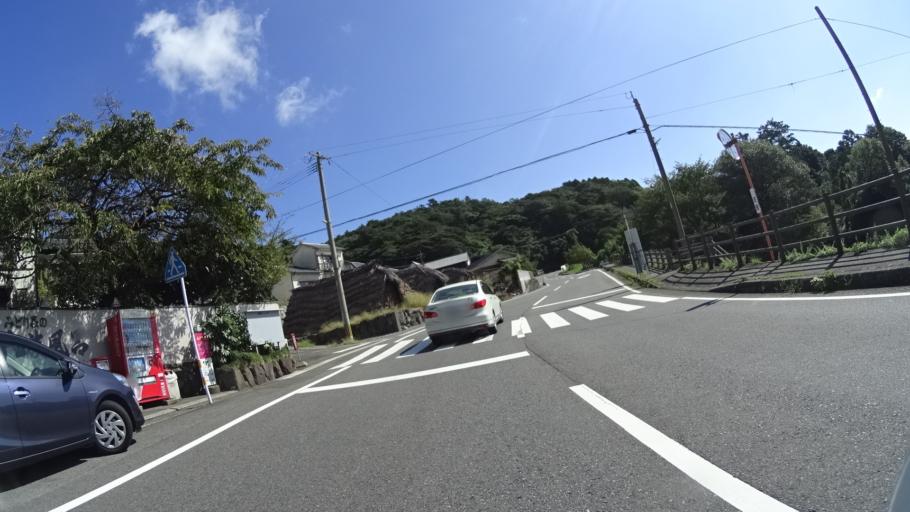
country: JP
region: Oita
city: Beppu
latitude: 33.3188
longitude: 131.4530
